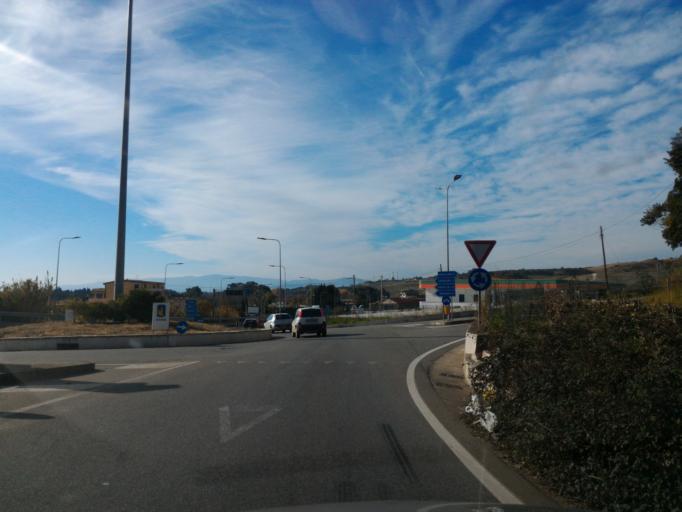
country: IT
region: Calabria
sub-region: Provincia di Catanzaro
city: Sellia Marina
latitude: 38.8856
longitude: 16.7131
